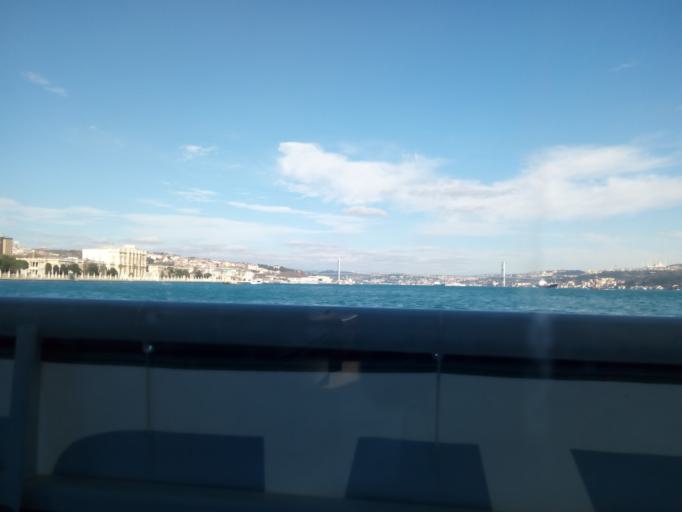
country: TR
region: Istanbul
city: Eminoenue
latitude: 41.0341
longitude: 28.9952
